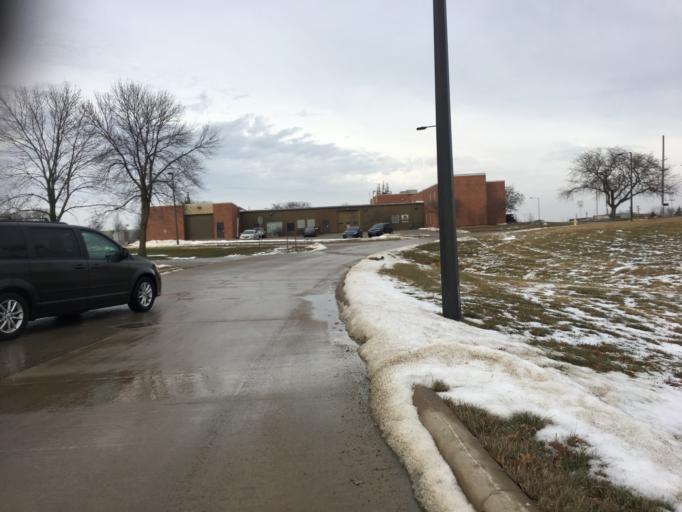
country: US
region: Iowa
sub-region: Johnson County
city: Coralville
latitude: 41.7062
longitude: -91.6049
